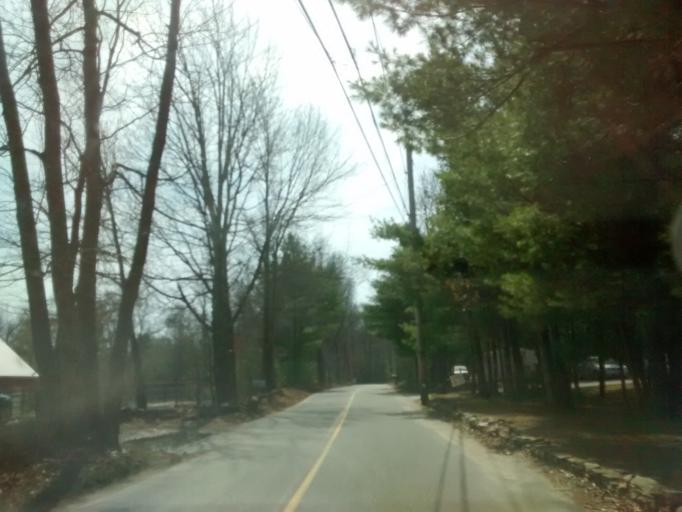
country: US
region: Massachusetts
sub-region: Worcester County
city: Southbridge
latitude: 42.1145
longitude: -72.0218
